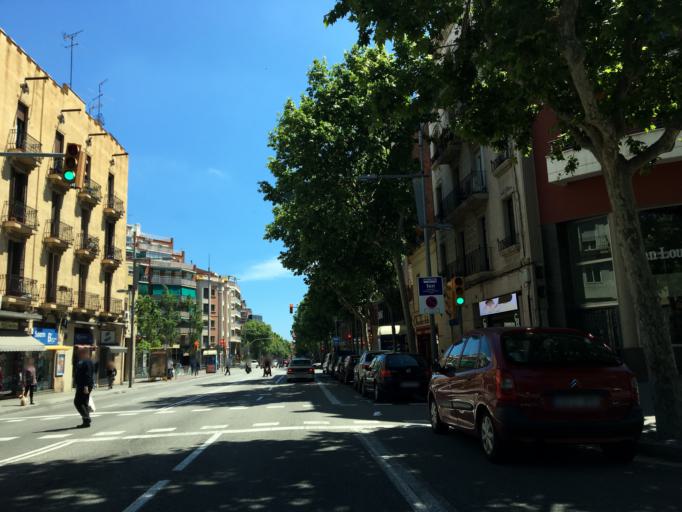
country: ES
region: Catalonia
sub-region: Provincia de Barcelona
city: Horta-Guinardo
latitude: 41.4250
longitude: 2.1765
